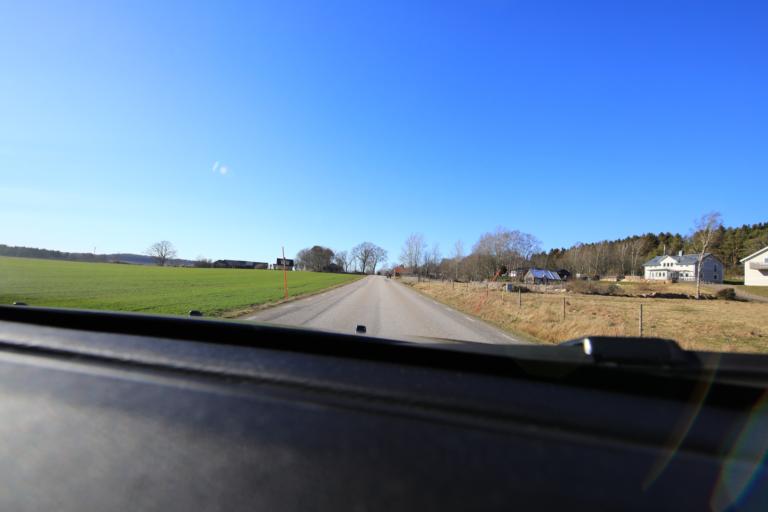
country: SE
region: Halland
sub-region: Varbergs Kommun
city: Tvaaker
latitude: 57.0605
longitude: 12.4296
